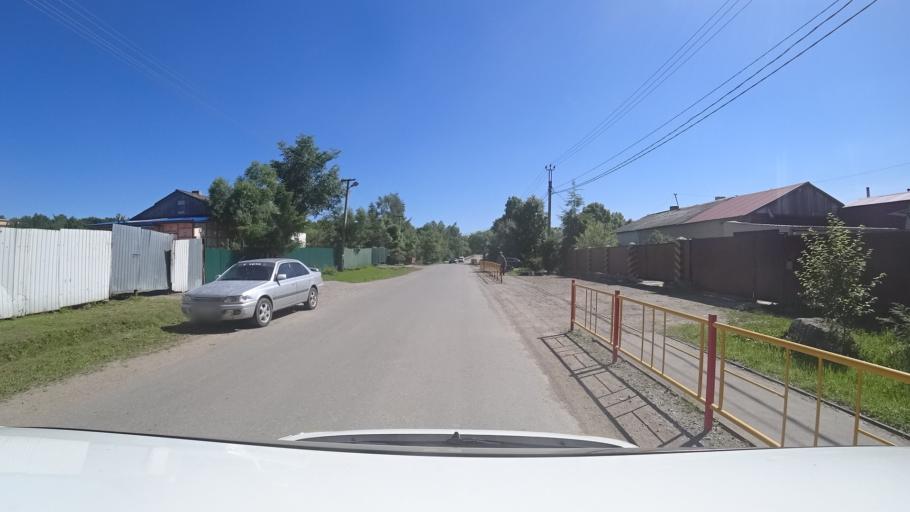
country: RU
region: Khabarovsk Krai
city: Topolevo
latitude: 48.5604
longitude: 135.1927
